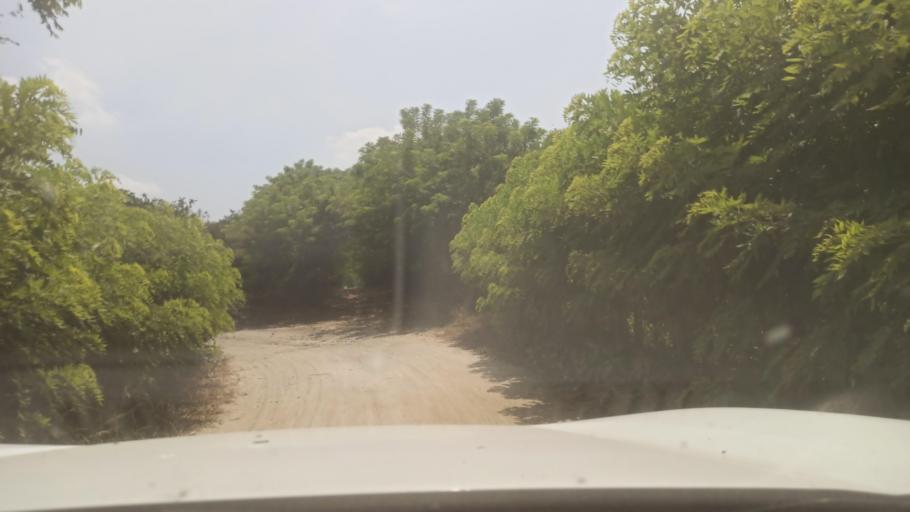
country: MX
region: Veracruz
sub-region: Atzalan
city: Colonias Pedernales
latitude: 20.0384
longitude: -97.0053
